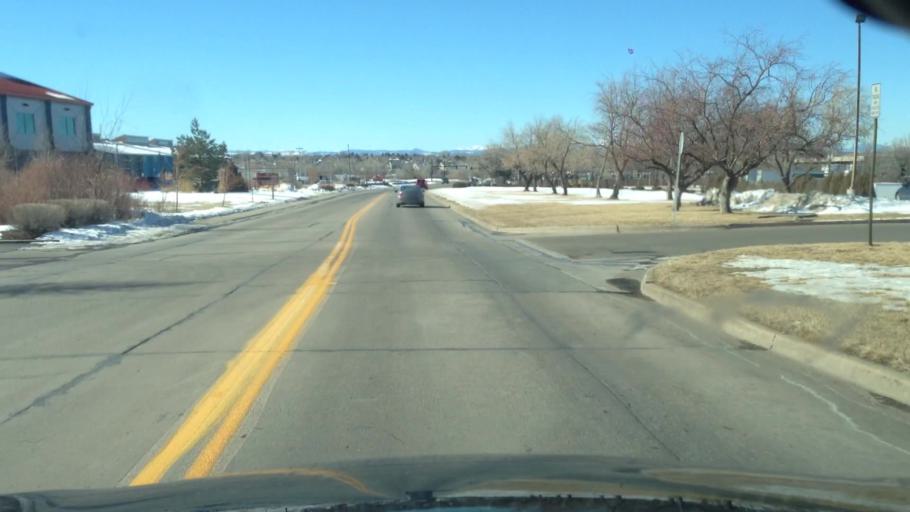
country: US
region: Colorado
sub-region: Douglas County
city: Parker
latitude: 39.5265
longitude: -104.7721
